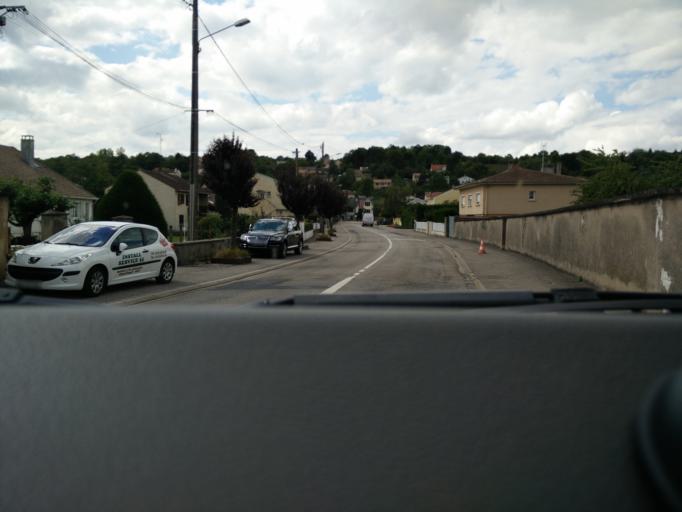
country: FR
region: Lorraine
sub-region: Departement de Meurthe-et-Moselle
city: Rosieres-aux-Salines
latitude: 48.5921
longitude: 6.3330
